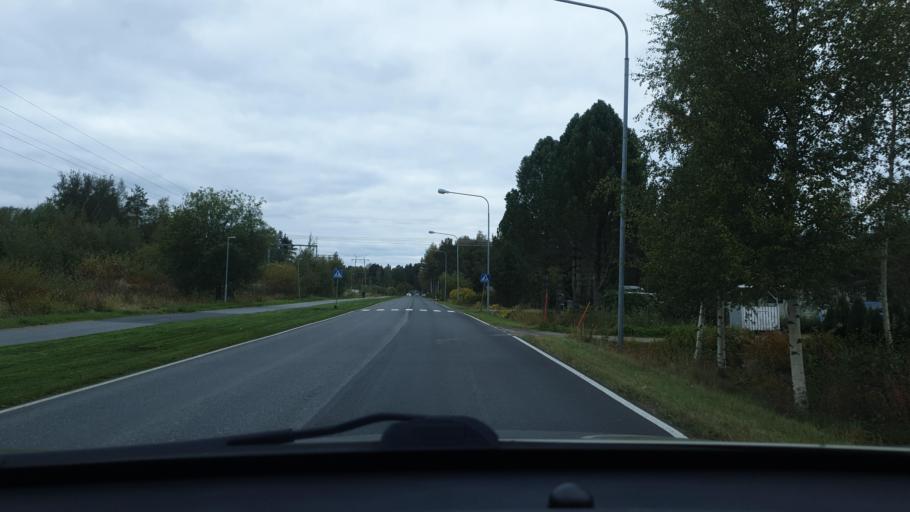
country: FI
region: Ostrobothnia
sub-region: Vaasa
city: Teeriniemi
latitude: 63.0909
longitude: 21.6994
